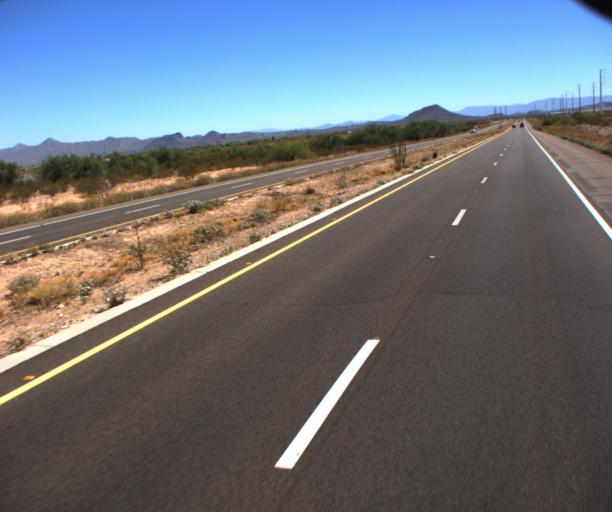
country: US
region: Arizona
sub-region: Maricopa County
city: Mesa
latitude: 33.4876
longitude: -111.8166
